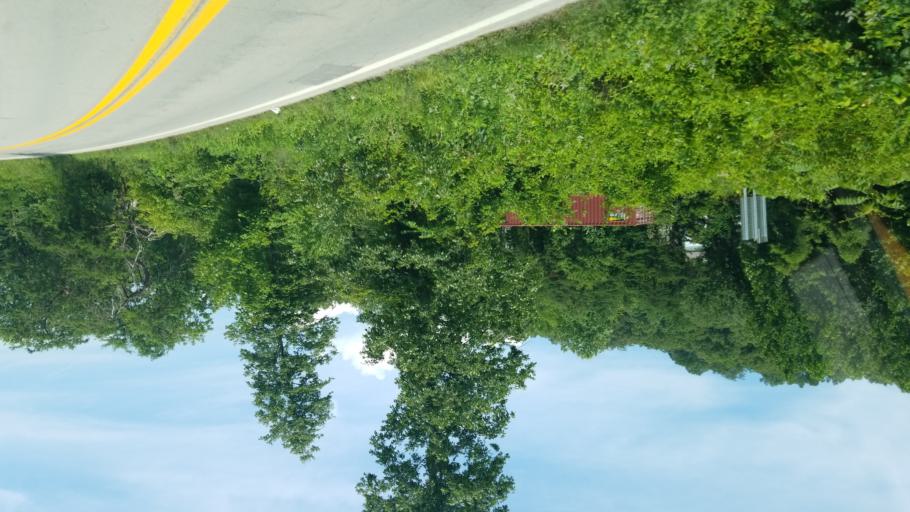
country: US
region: West Virginia
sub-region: Putnam County
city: Teays Valley
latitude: 38.4553
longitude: -81.8877
